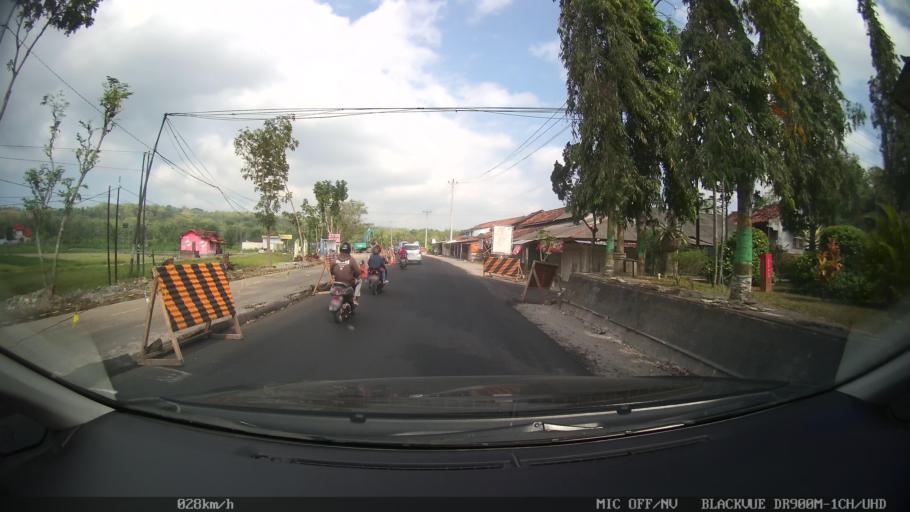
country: ID
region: Daerah Istimewa Yogyakarta
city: Srandakan
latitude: -7.8686
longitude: 110.1912
